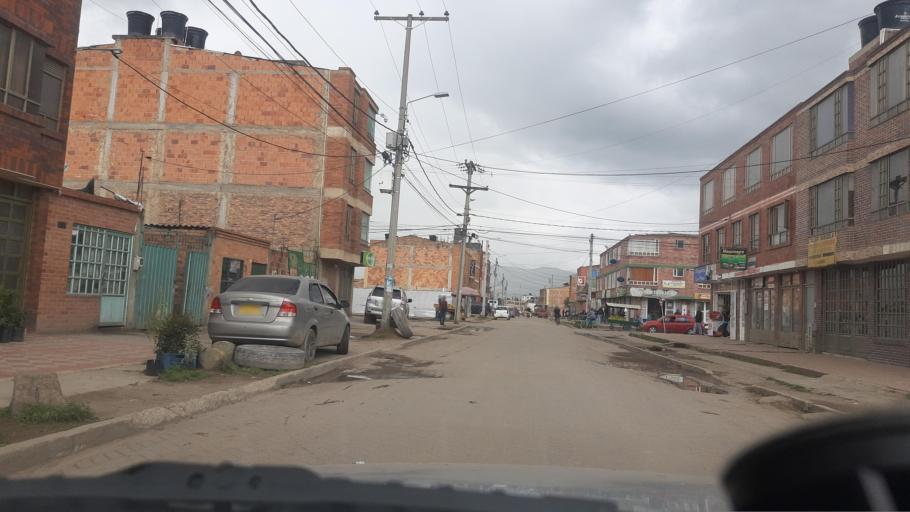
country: CO
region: Cundinamarca
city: Ubate
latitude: 5.3125
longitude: -73.8097
